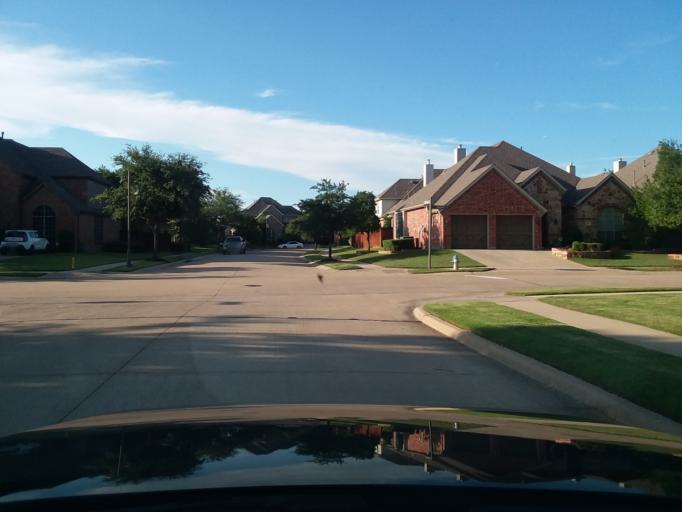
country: US
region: Texas
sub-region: Denton County
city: Copper Canyon
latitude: 33.1048
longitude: -97.1208
